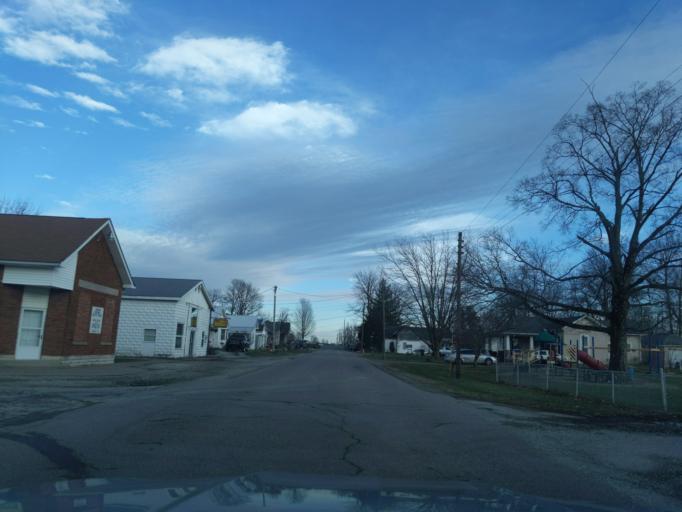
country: US
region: Indiana
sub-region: Decatur County
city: Westport
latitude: 39.2347
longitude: -85.5647
